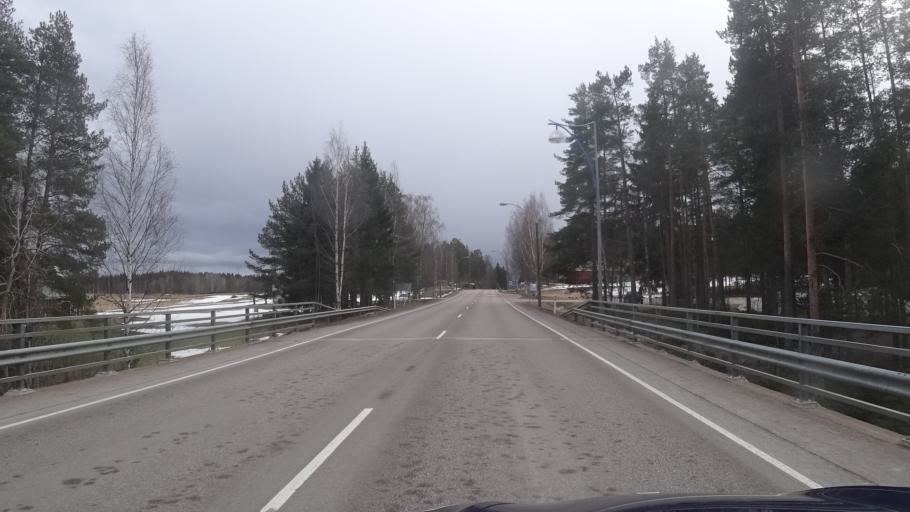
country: FI
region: Kymenlaakso
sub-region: Kouvola
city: Anjala
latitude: 60.6749
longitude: 26.7672
